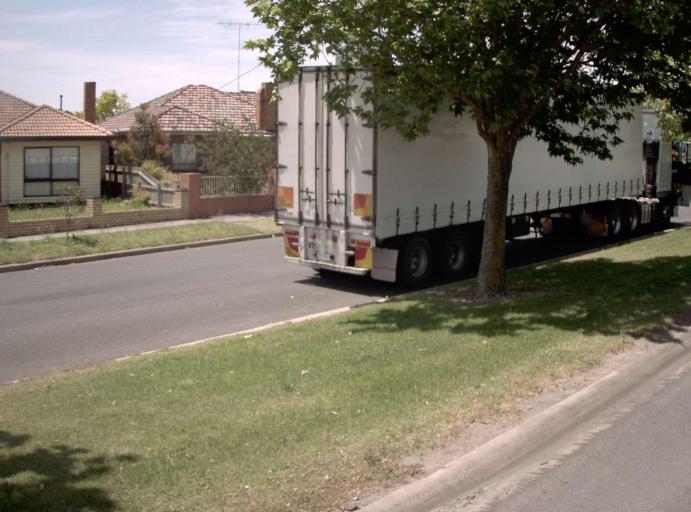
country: AU
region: Victoria
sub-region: Latrobe
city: Traralgon
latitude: -38.1919
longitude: 146.5539
